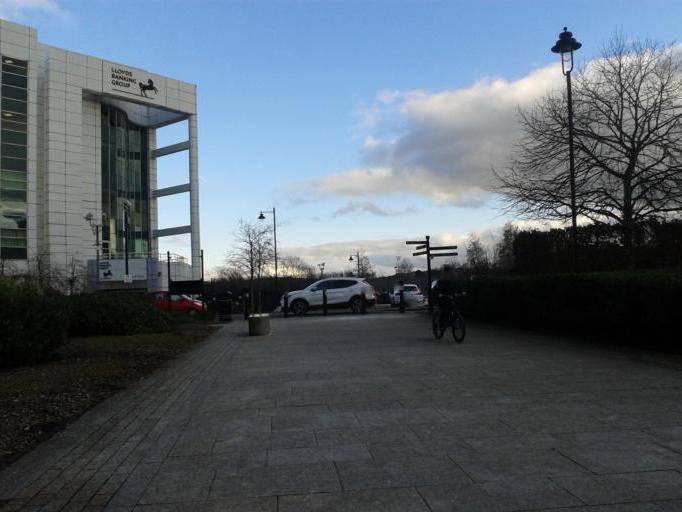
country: GB
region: Northern Ireland
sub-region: City of Belfast
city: Belfast
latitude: 54.5912
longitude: -5.9224
